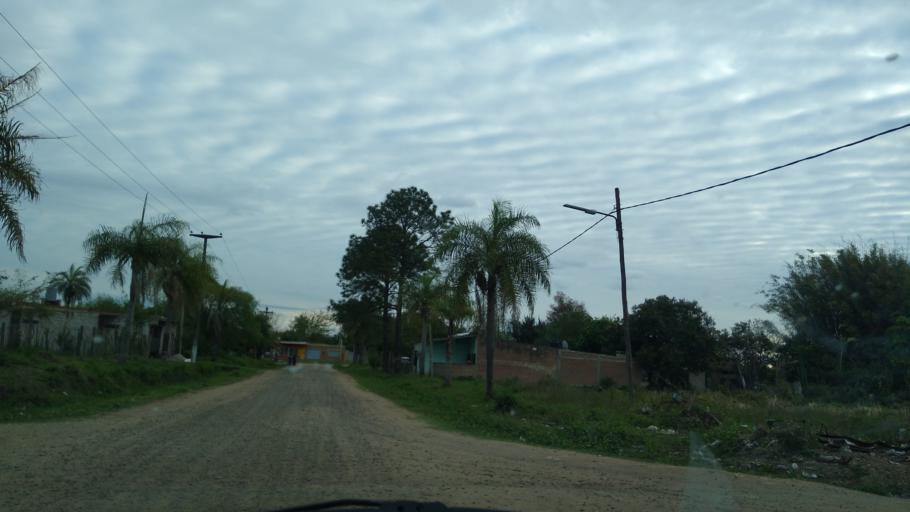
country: AR
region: Chaco
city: Fontana
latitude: -27.4017
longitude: -59.0402
